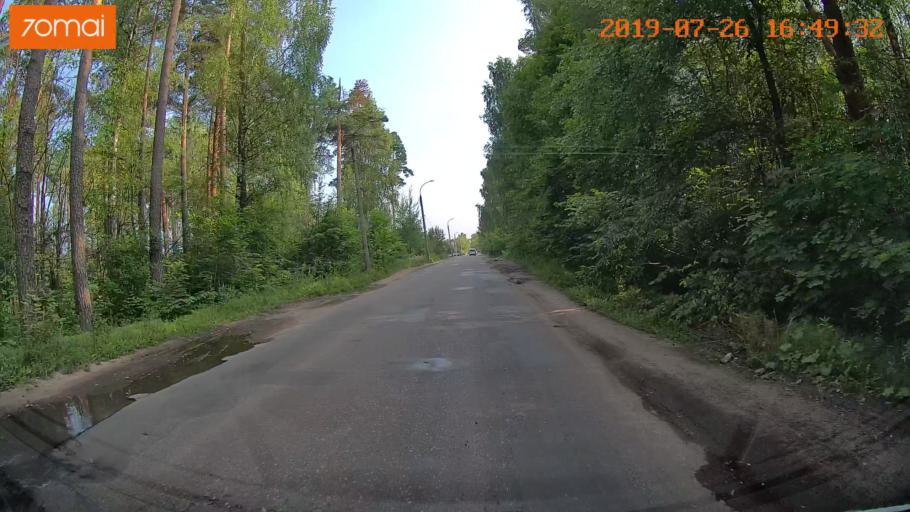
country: RU
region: Ivanovo
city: Bogorodskoye
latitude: 57.0287
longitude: 41.0207
